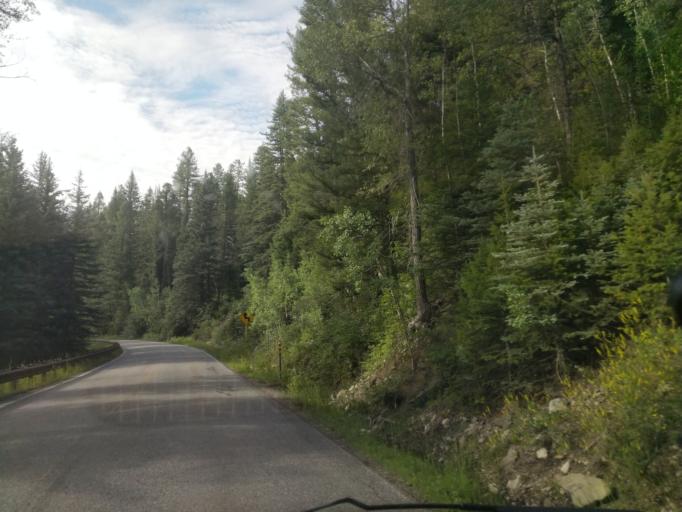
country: US
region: Colorado
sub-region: Garfield County
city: Carbondale
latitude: 39.1085
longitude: -107.2663
